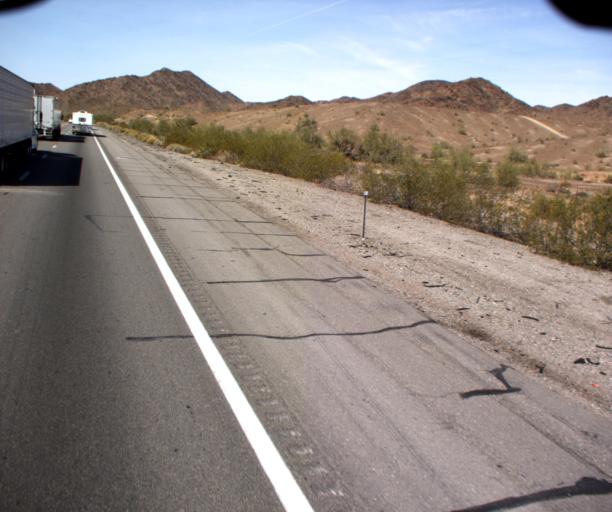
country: US
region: Arizona
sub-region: La Paz County
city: Quartzsite
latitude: 33.6481
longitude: -114.3502
